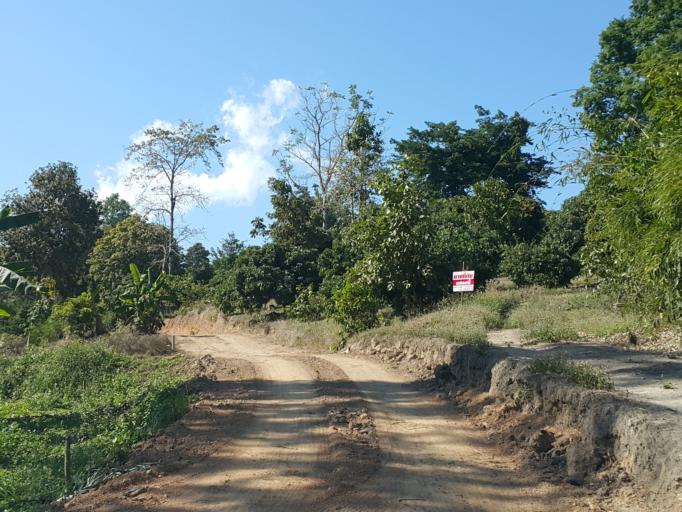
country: TH
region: Chiang Mai
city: Mae Taeng
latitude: 18.9587
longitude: 98.9041
